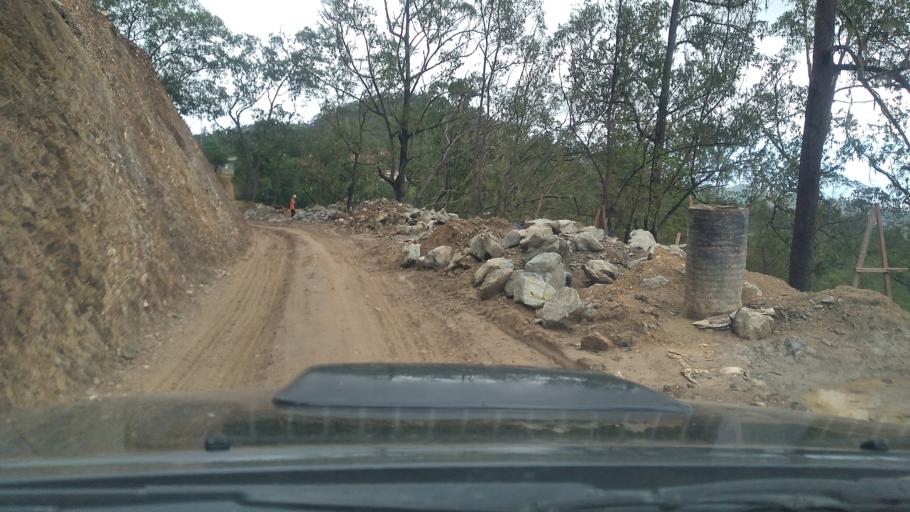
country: TL
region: Dili
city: Dili
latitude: -8.6301
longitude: 125.6252
